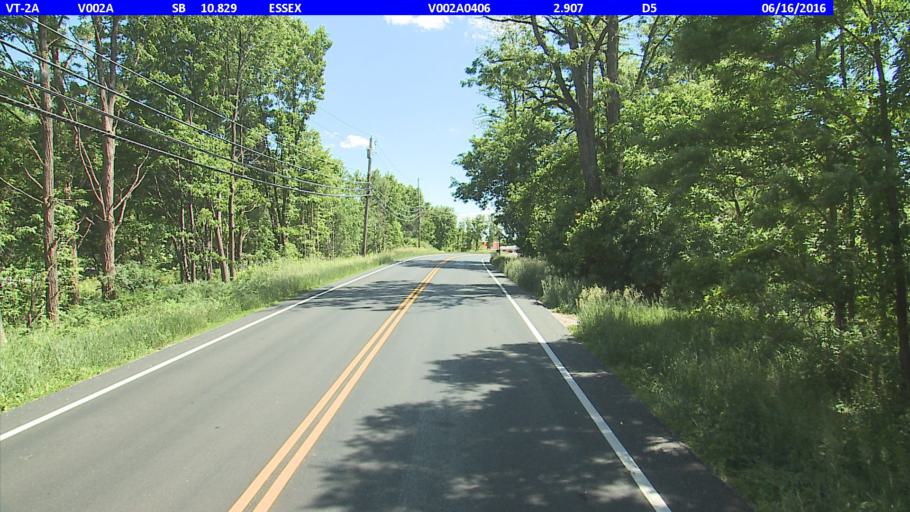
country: US
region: Vermont
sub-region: Chittenden County
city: Essex Junction
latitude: 44.5212
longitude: -73.1235
